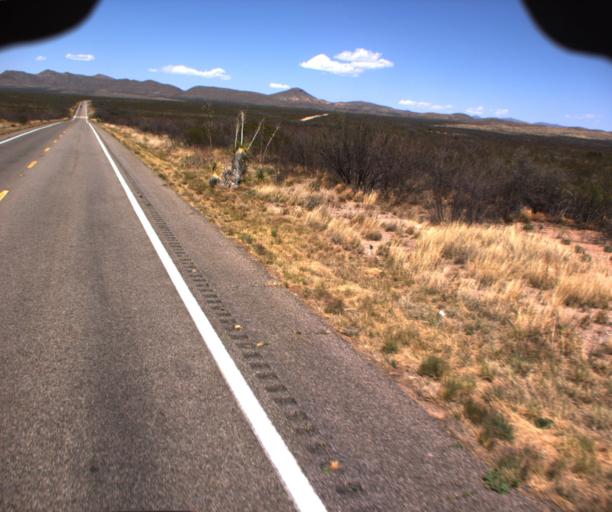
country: US
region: Arizona
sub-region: Cochise County
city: Tombstone
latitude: 31.6057
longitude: -110.0490
